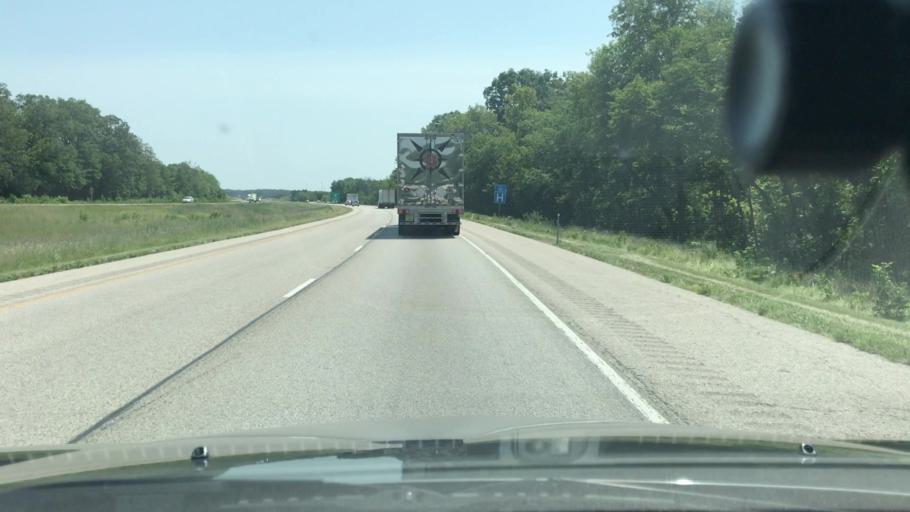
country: US
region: Illinois
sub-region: Washington County
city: Nashville
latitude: 38.3930
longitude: -89.3829
